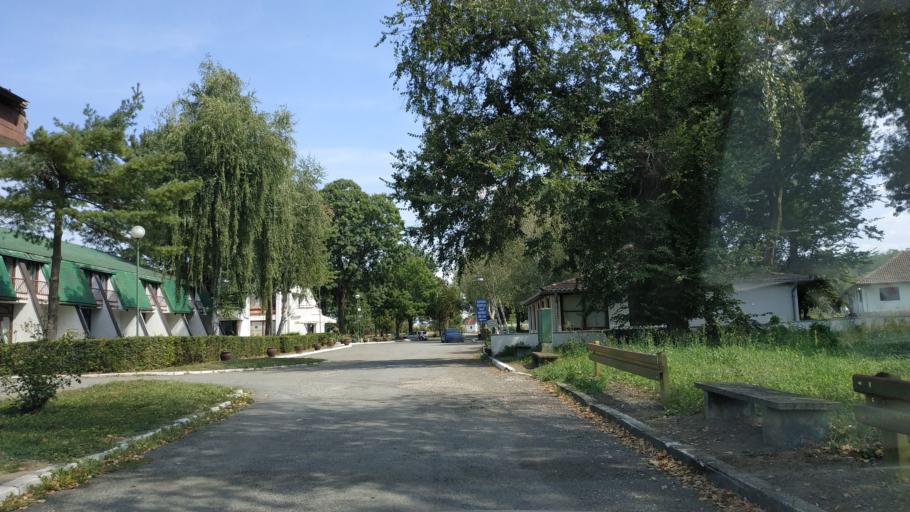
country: RS
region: Central Serbia
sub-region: Belgrade
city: Grocka
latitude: 44.5829
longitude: 20.8169
